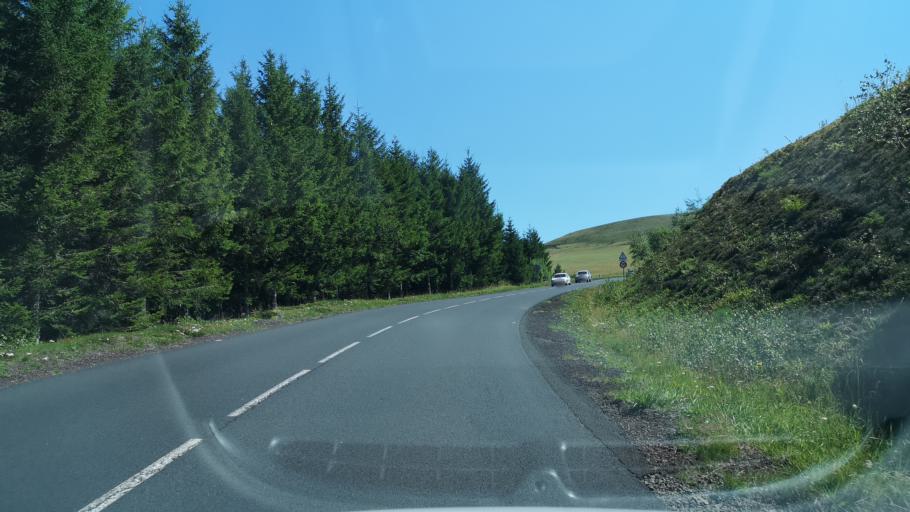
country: FR
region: Auvergne
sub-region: Departement du Puy-de-Dome
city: Mont-Dore
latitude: 45.6001
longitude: 2.8411
